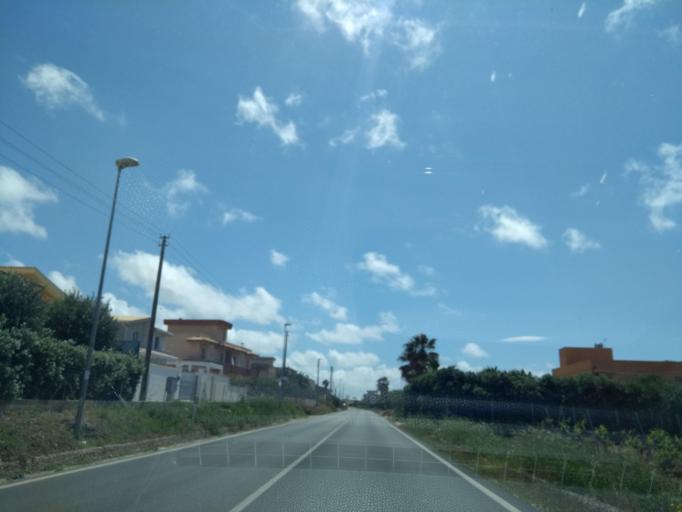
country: IT
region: Sicily
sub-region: Trapani
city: Marsala
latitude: 37.8690
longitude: 12.5181
